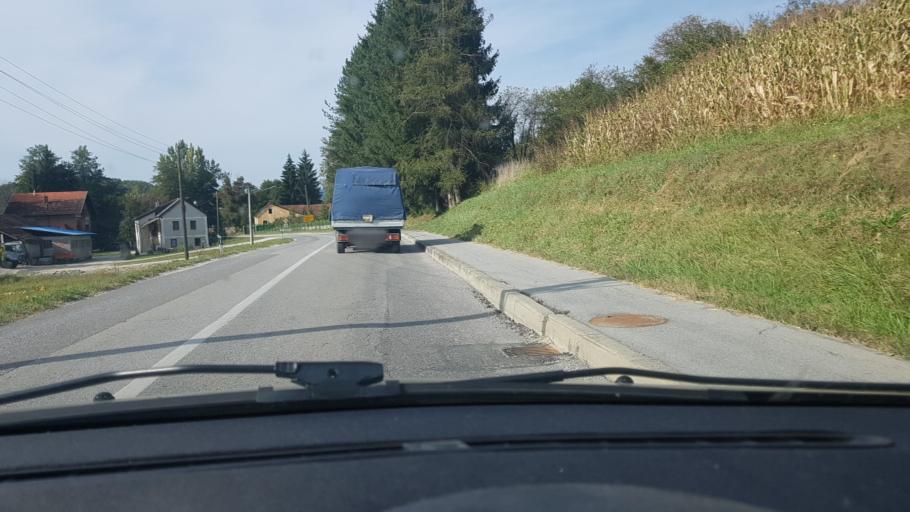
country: HR
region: Krapinsko-Zagorska
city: Zlatar
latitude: 46.0980
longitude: 16.0357
